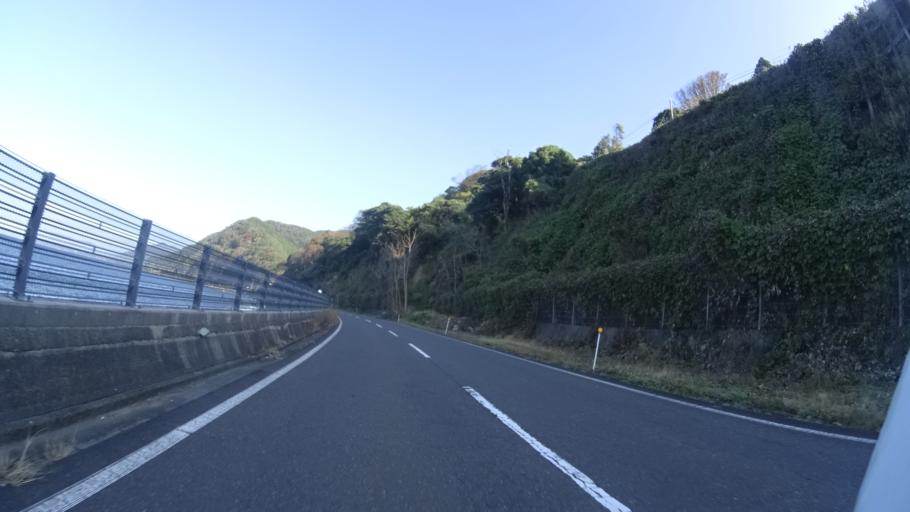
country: JP
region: Fukui
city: Tsuruga
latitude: 35.7529
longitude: 136.1015
